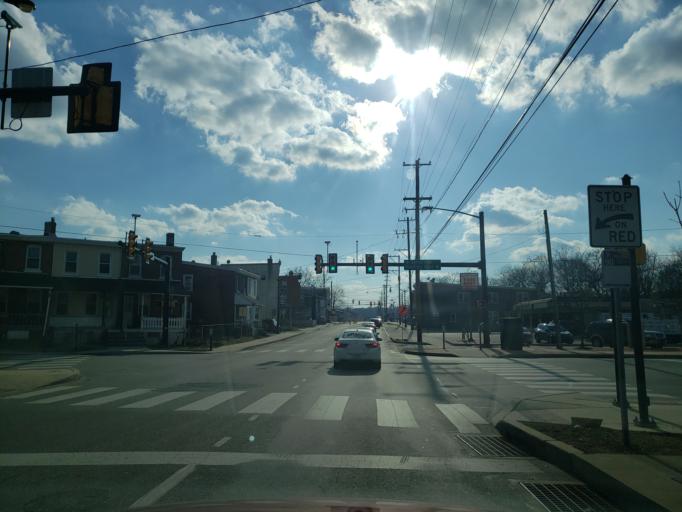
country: US
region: Pennsylvania
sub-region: Montgomery County
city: Norristown
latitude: 40.1231
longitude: -75.3425
